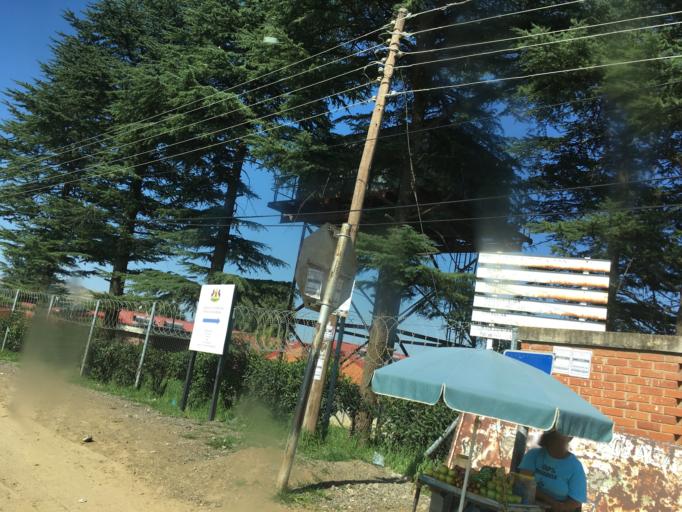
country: LS
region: Butha-Buthe
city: Butha-Buthe
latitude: -28.7658
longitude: 28.2471
